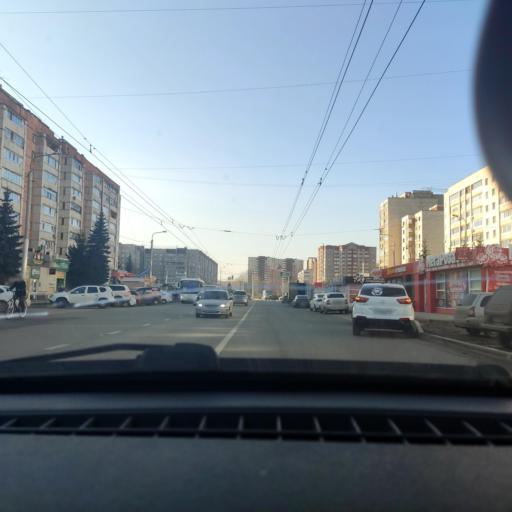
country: RU
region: Bashkortostan
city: Ufa
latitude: 54.7802
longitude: 56.1197
